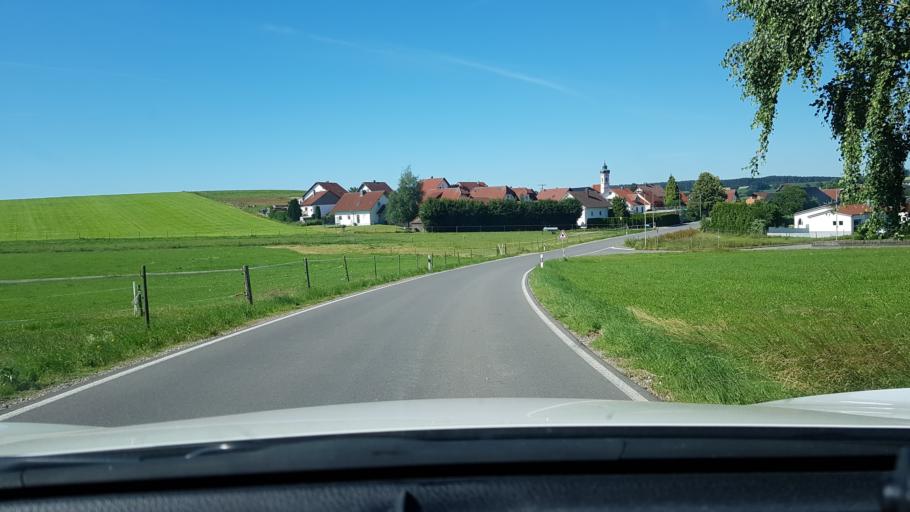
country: DE
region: Baden-Wuerttemberg
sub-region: Tuebingen Region
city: Gutenzell-Hurbel
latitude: 48.1137
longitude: 9.9533
